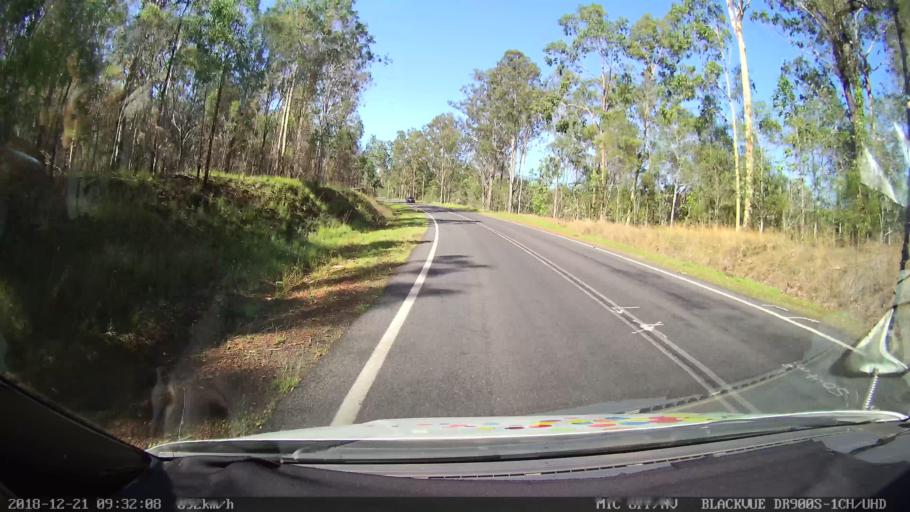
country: AU
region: New South Wales
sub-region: Clarence Valley
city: Maclean
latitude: -29.4668
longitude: 152.9803
